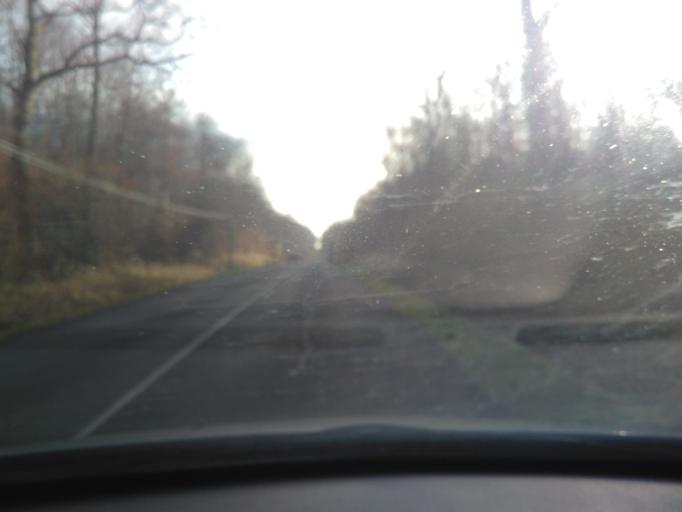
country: FR
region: Bourgogne
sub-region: Departement de la Nievre
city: Saint-Parize-le-Chatel
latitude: 46.8007
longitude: 3.2689
